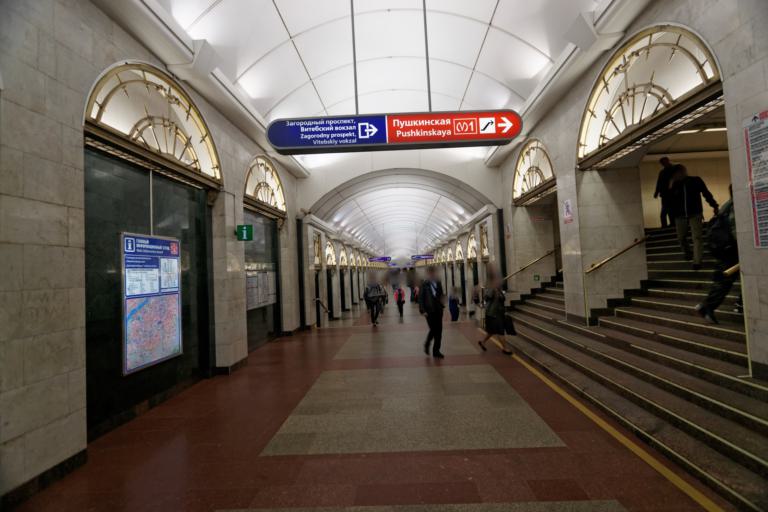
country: RU
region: St.-Petersburg
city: Saint Petersburg
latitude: 59.9222
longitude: 30.3352
